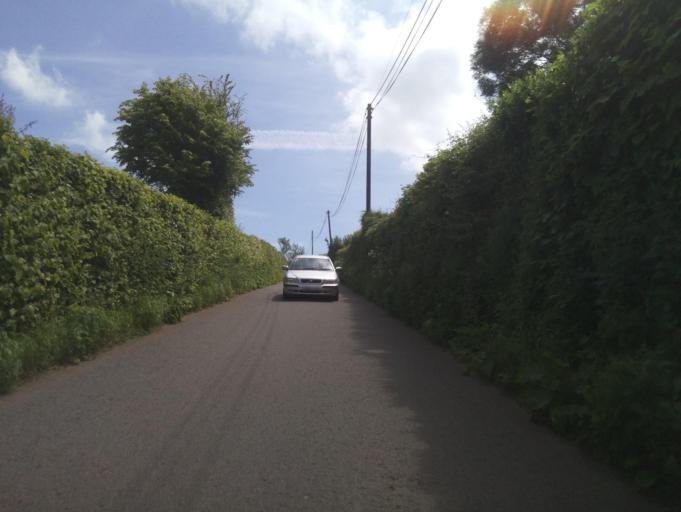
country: GB
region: England
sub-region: Herefordshire
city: Llanrothal
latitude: 51.8709
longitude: -2.8040
